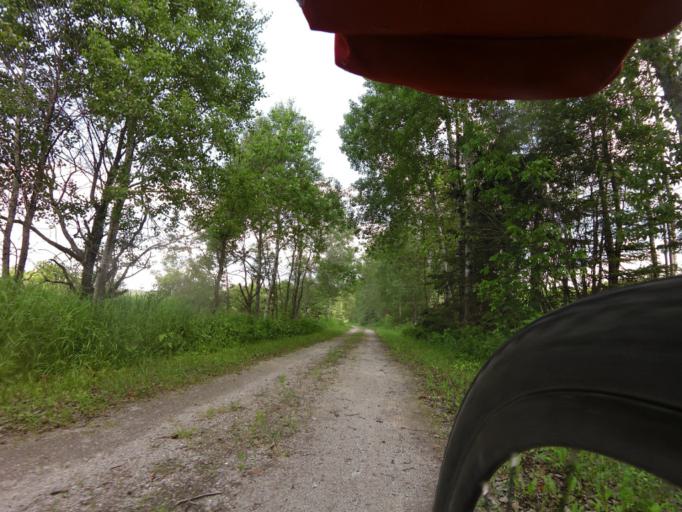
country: CA
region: Quebec
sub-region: Outaouais
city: Maniwaki
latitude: 46.0702
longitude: -76.0985
